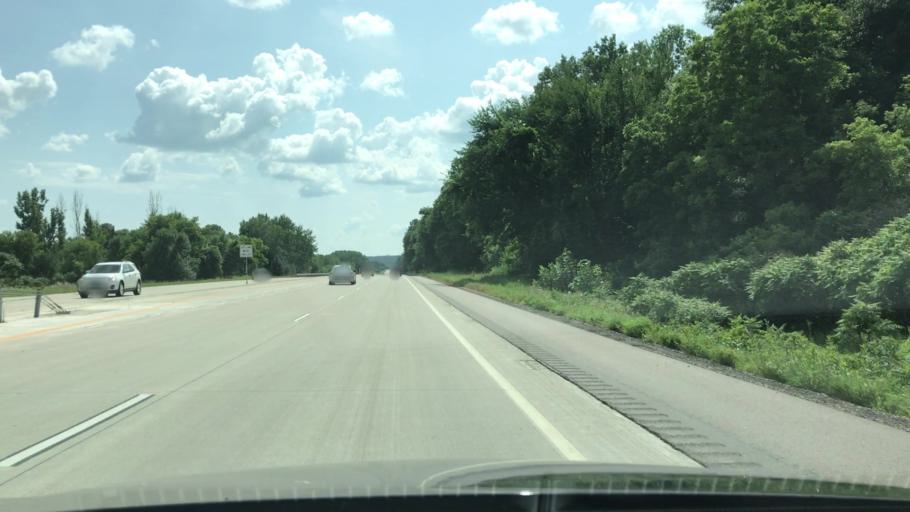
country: US
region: Minnesota
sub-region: Nicollet County
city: Saint Peter
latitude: 44.2899
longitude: -94.0000
